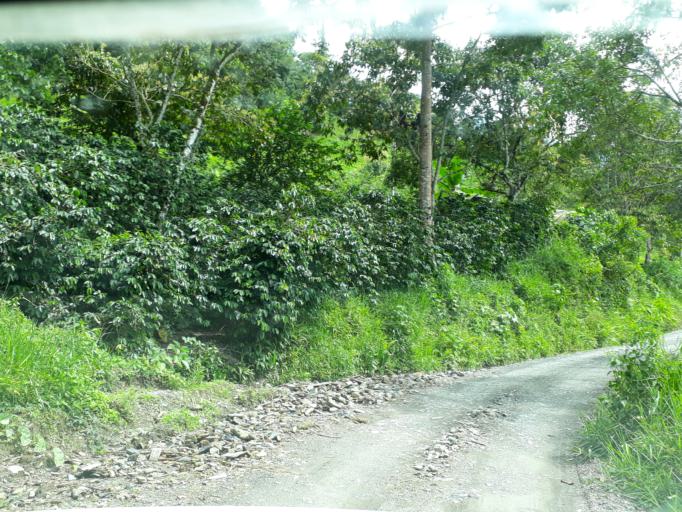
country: CO
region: Boyaca
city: Quipama
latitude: 5.4367
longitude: -74.1812
